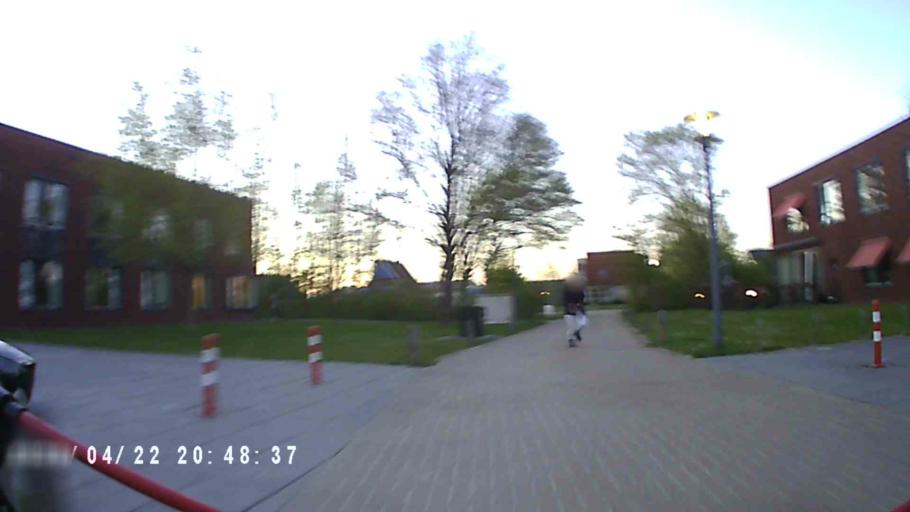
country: NL
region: Groningen
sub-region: Gemeente Winsum
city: Winsum
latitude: 53.3306
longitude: 6.5286
